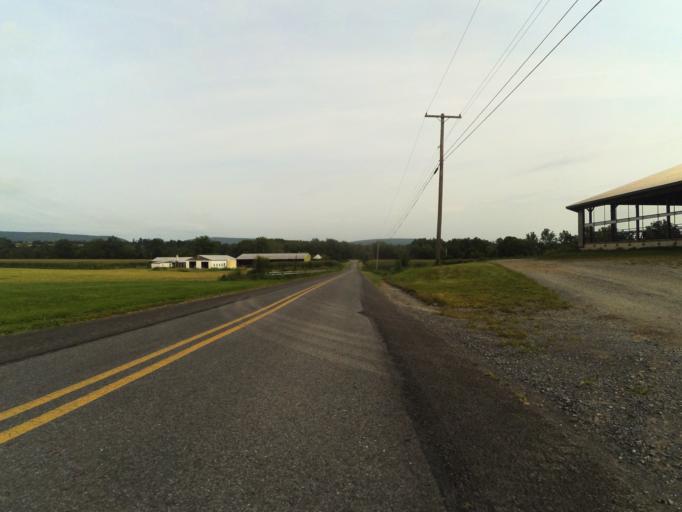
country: US
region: Pennsylvania
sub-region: Huntingdon County
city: Huntingdon
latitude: 40.5581
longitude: -78.0682
